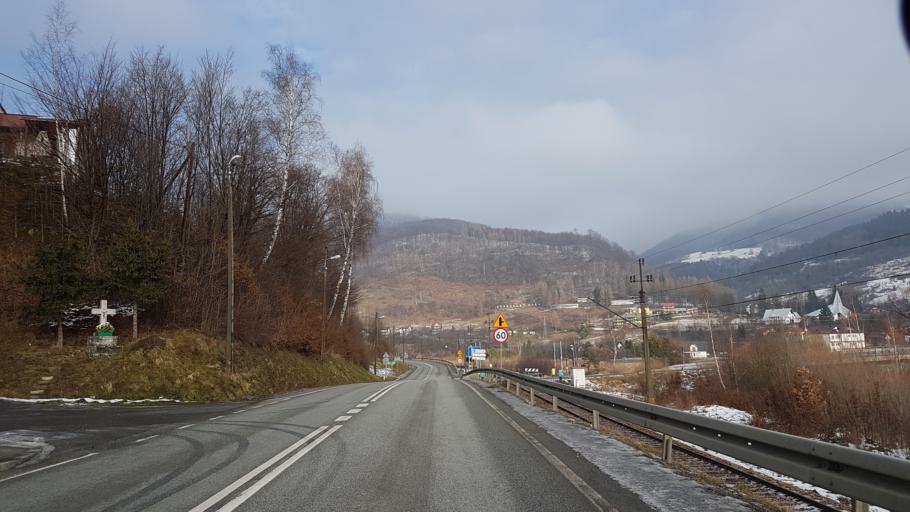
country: PL
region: Lesser Poland Voivodeship
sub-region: Powiat nowosadecki
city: Piwniczna-Zdroj
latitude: 49.4644
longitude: 20.6969
